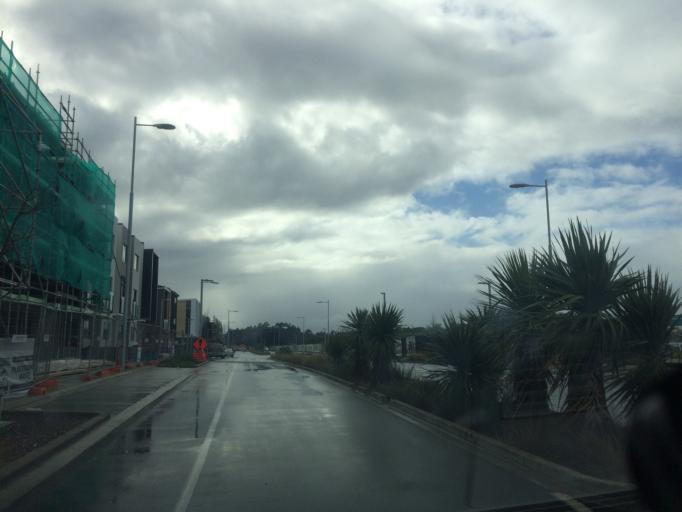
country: NZ
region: Auckland
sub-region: Auckland
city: Rosebank
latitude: -36.7921
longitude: 174.6621
